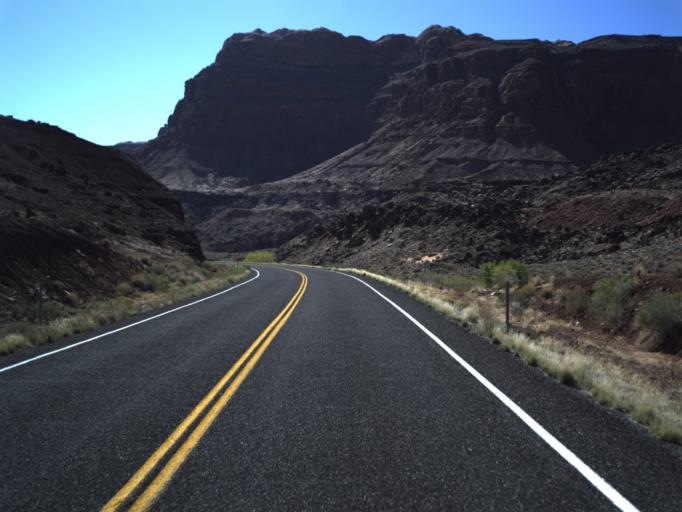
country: US
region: Utah
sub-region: San Juan County
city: Blanding
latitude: 37.9016
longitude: -110.4500
